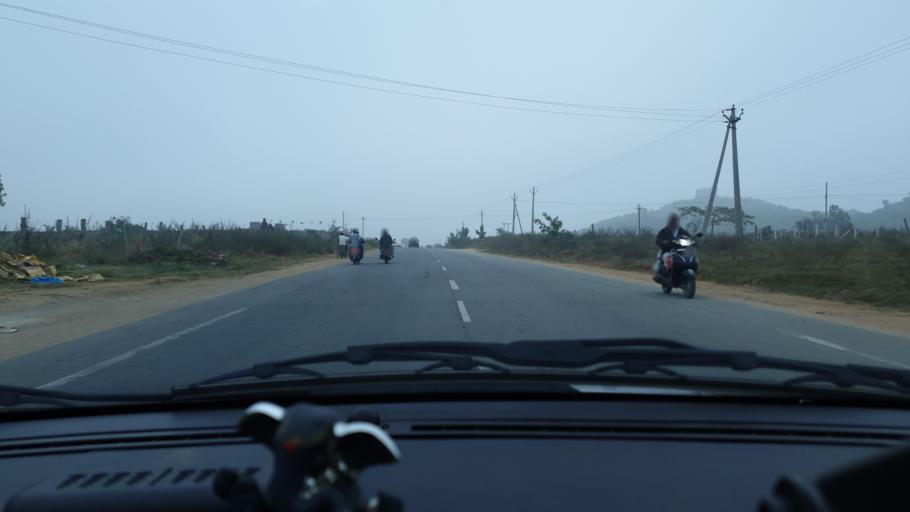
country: IN
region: Telangana
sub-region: Mahbubnagar
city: Farrukhnagar
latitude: 16.9443
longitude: 78.5248
